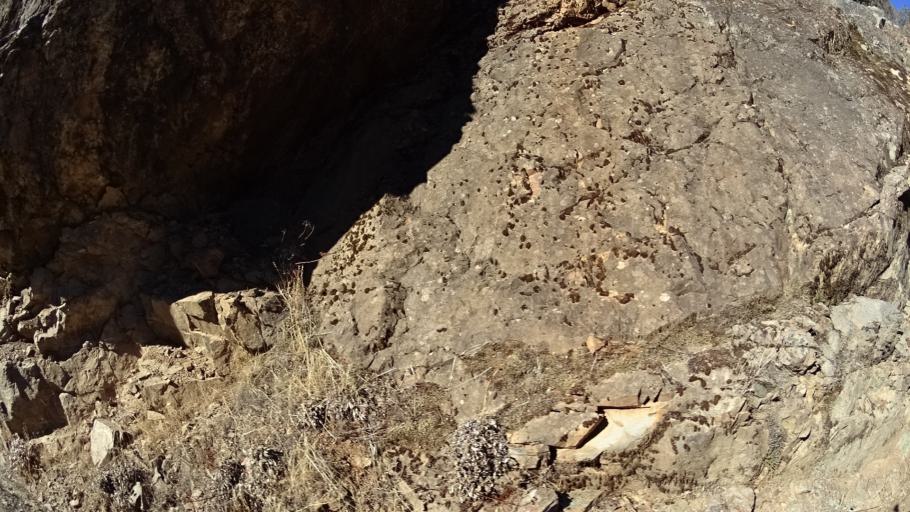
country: US
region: California
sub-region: Siskiyou County
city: Happy Camp
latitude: 41.2976
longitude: -123.0896
